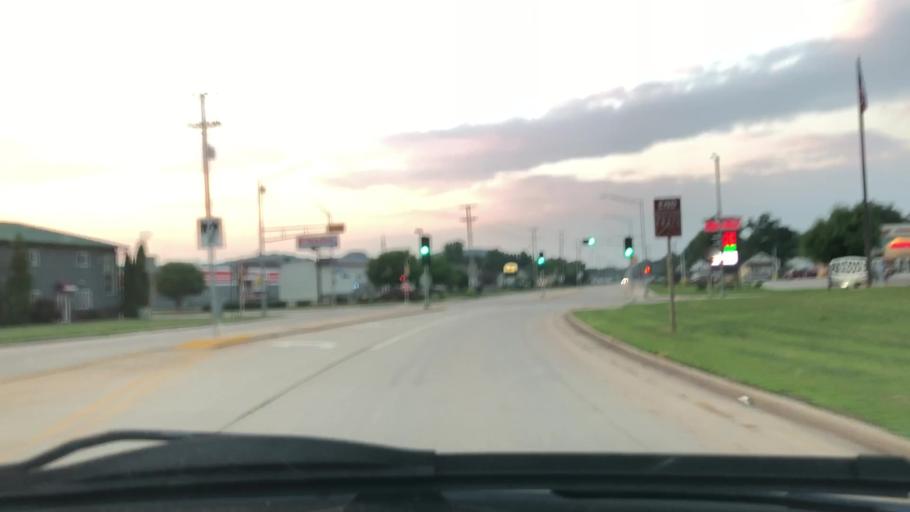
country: US
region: Wisconsin
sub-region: Richland County
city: Richland Center
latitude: 43.3341
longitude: -90.3890
